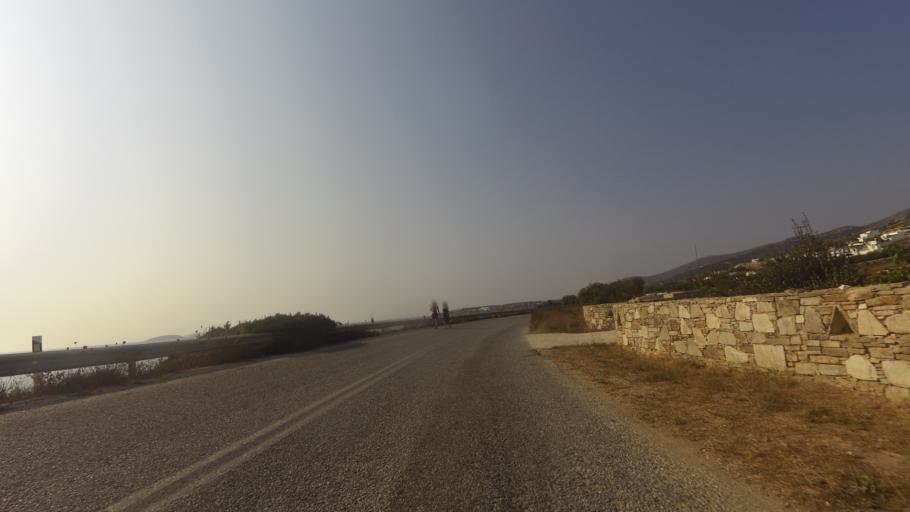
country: GR
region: South Aegean
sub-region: Nomos Kykladon
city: Antiparos
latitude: 37.0155
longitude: 25.0754
